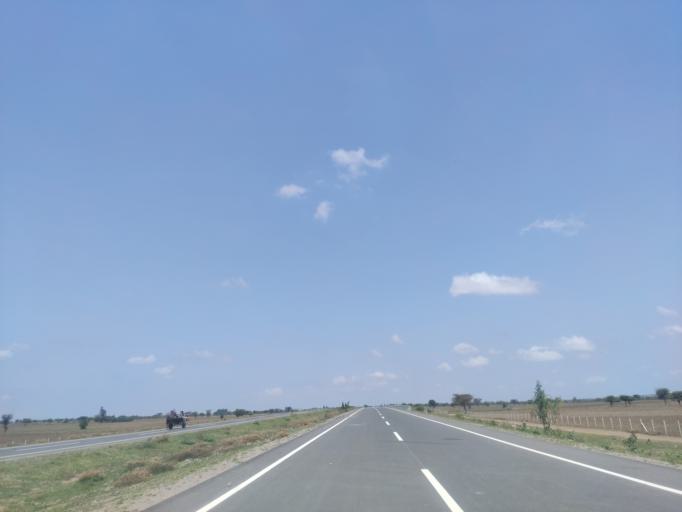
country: ET
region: Oromiya
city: Mojo
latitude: 8.2918
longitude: 38.9247
